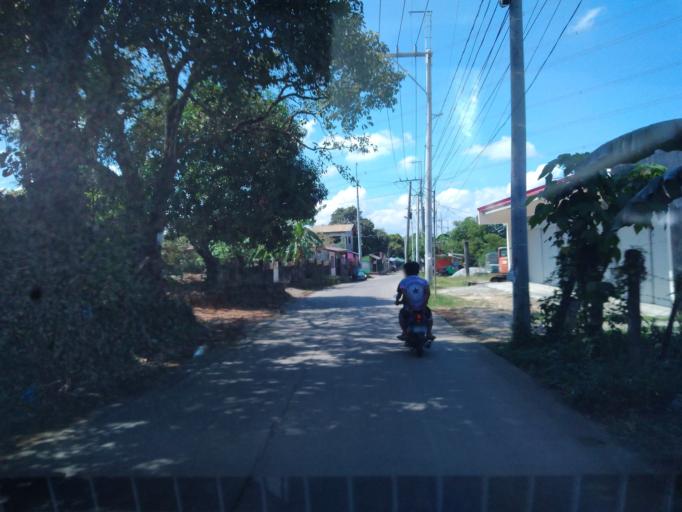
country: PH
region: Central Luzon
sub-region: Province of Bulacan
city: Balasing
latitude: 14.8597
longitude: 121.0337
